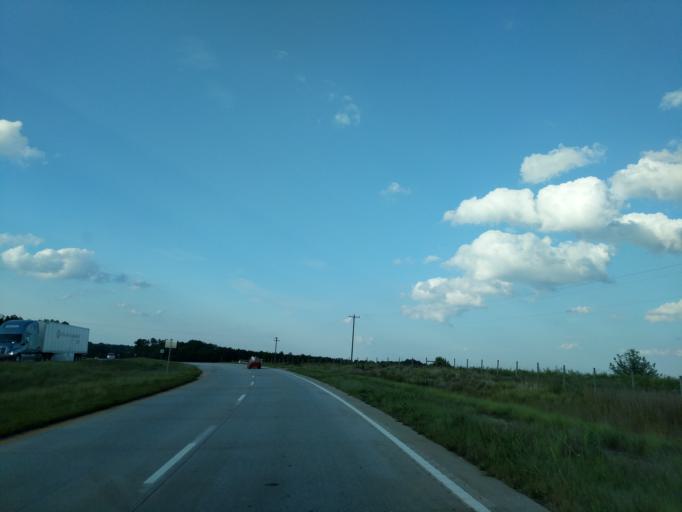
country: US
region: South Carolina
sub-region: Greenville County
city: Greer
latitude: 34.9015
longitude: -82.2197
